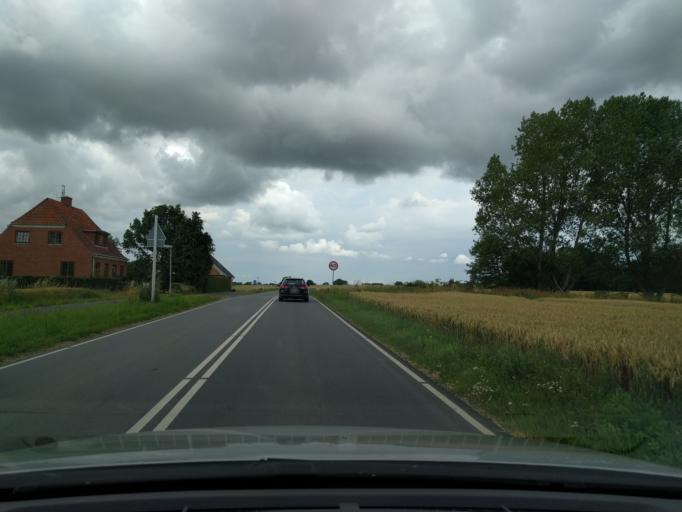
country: DK
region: South Denmark
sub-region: Nyborg Kommune
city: Ullerslev
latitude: 55.3647
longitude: 10.7257
